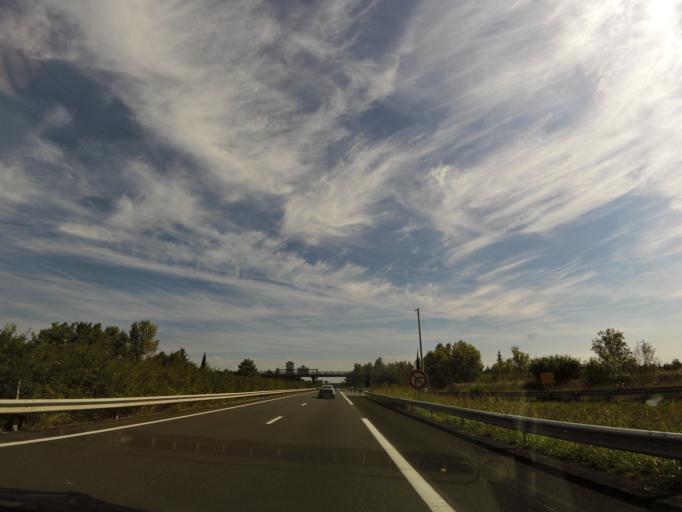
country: FR
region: Languedoc-Roussillon
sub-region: Departement du Gard
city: Nimes
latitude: 43.8079
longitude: 4.3524
